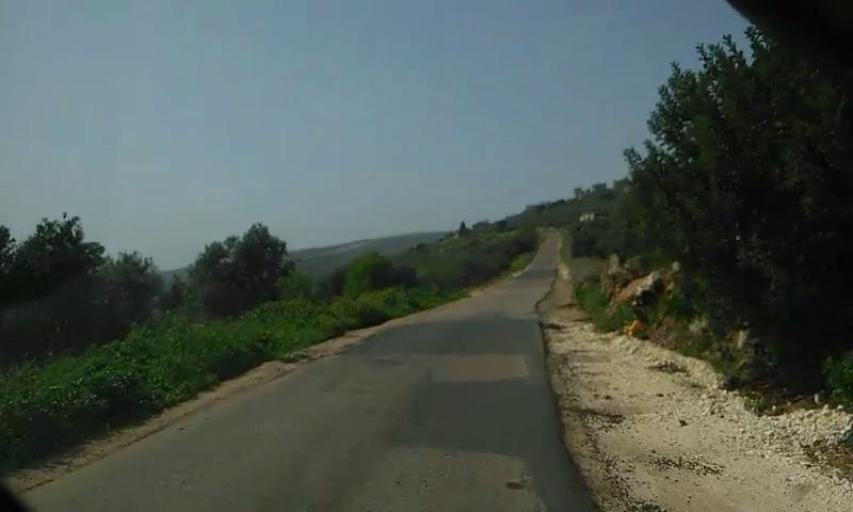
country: PS
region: West Bank
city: `Anin
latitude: 32.4972
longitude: 35.1833
